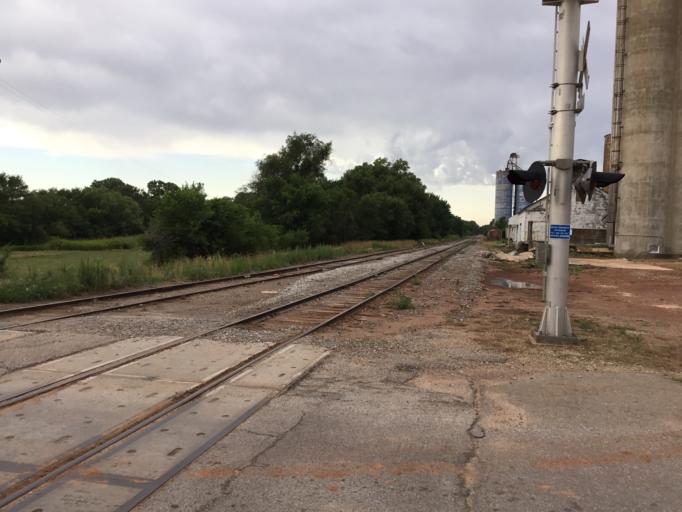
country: US
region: Kansas
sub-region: Kingman County
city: Kingman
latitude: 37.6416
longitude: -98.1132
